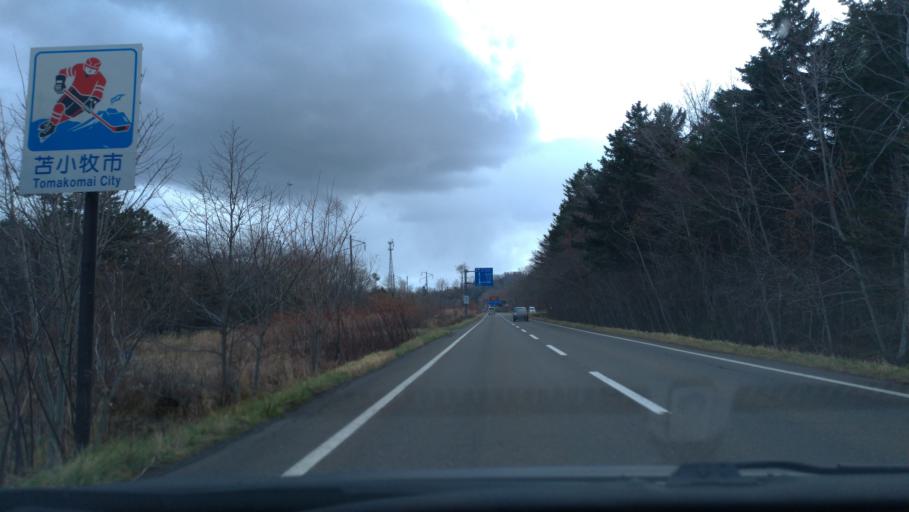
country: JP
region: Hokkaido
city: Tomakomai
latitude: 42.7600
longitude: 141.4377
